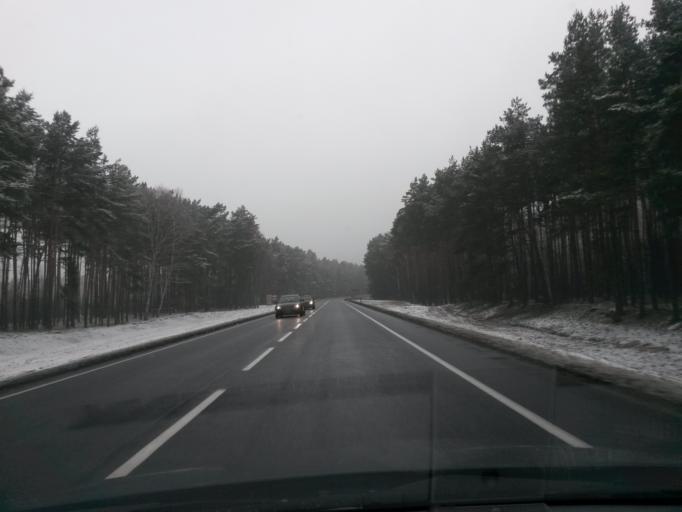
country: PL
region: Kujawsko-Pomorskie
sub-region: Powiat bydgoski
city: Biale Blota
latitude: 53.1049
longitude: 17.8874
